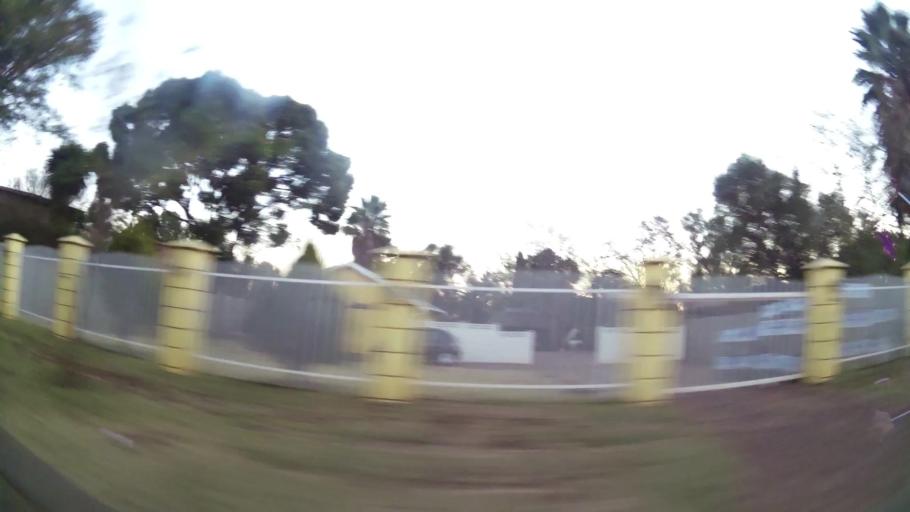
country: ZA
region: Gauteng
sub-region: City of Tshwane Metropolitan Municipality
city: Centurion
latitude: -25.8571
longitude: 28.1341
